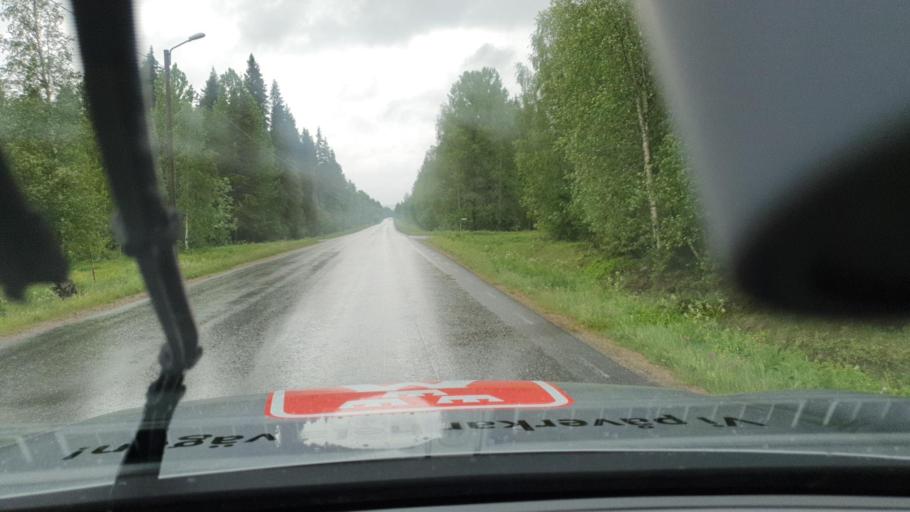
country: FI
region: Lapland
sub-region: Torniolaakso
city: Ylitornio
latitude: 66.2490
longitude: 23.6702
